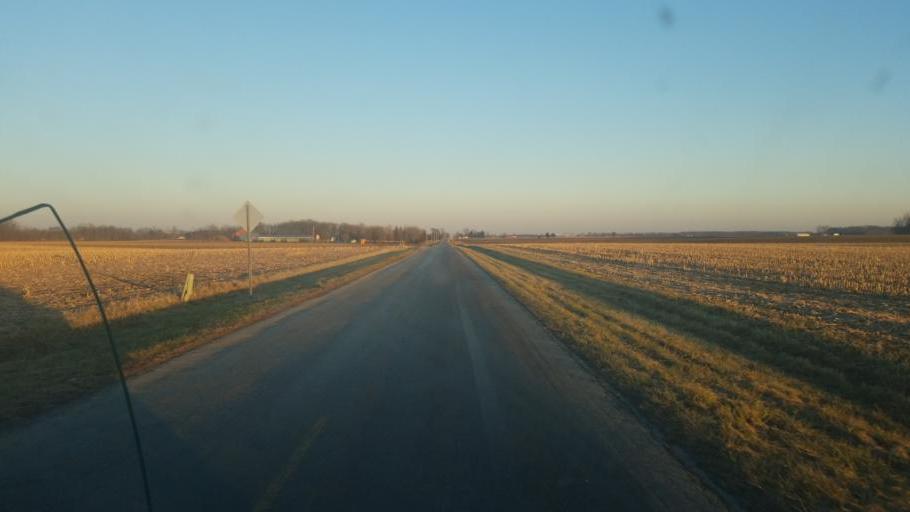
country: US
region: Ohio
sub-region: Union County
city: Richwood
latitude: 40.6219
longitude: -83.3782
